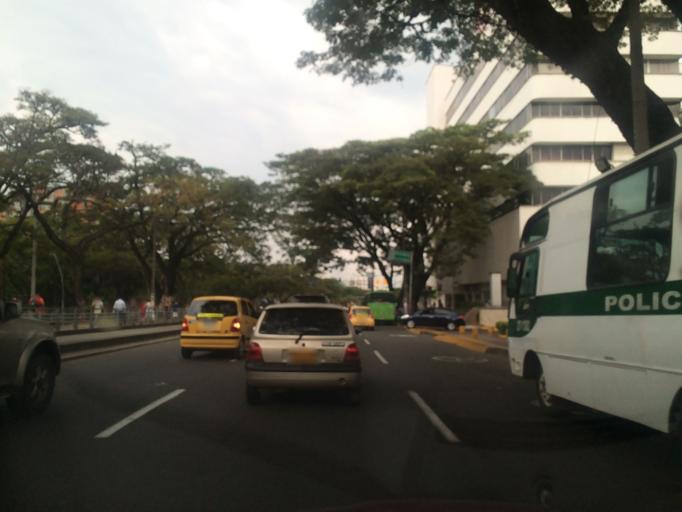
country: CO
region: Valle del Cauca
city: Cali
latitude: 3.3723
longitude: -76.5396
